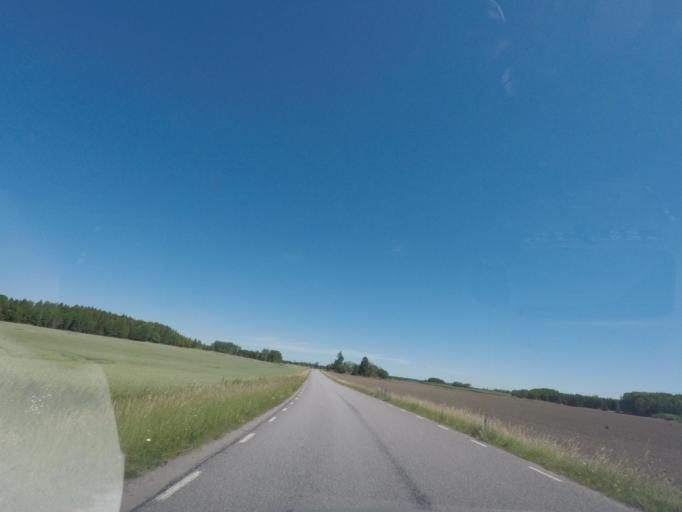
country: SE
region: Uppsala
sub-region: Enkopings Kommun
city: Irsta
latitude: 59.6764
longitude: 16.9436
